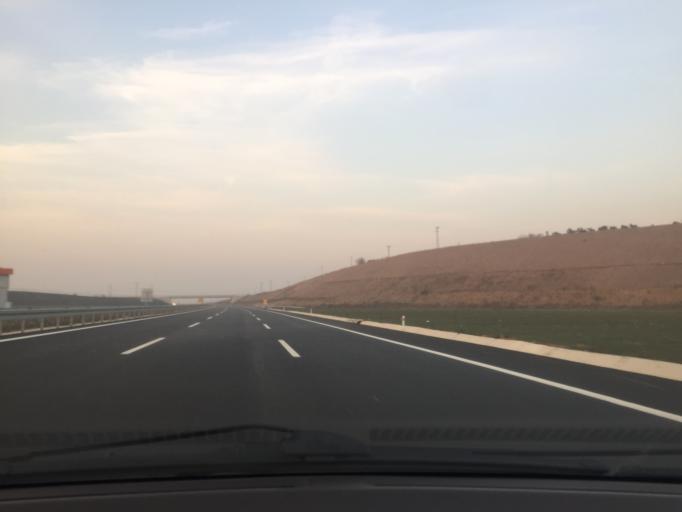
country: TR
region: Bursa
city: Karacabey
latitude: 40.2461
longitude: 28.4372
